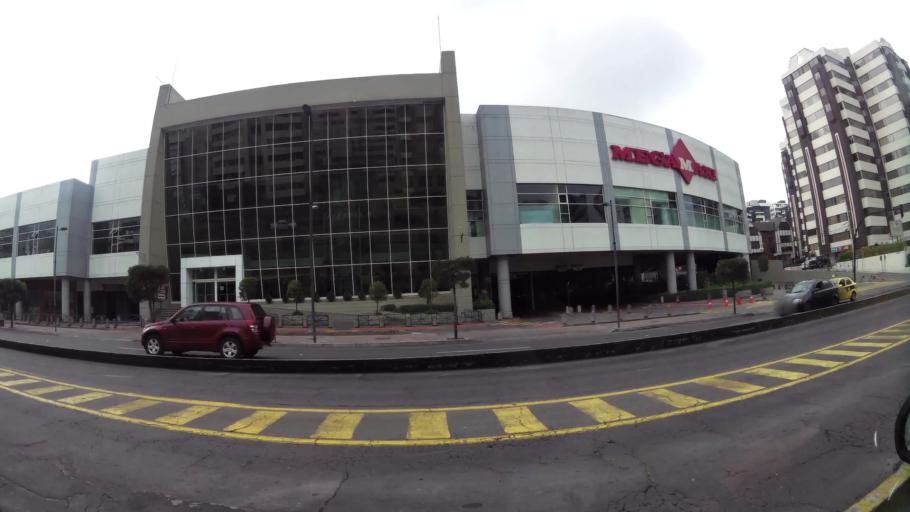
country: EC
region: Pichincha
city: Quito
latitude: -0.1804
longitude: -78.4785
